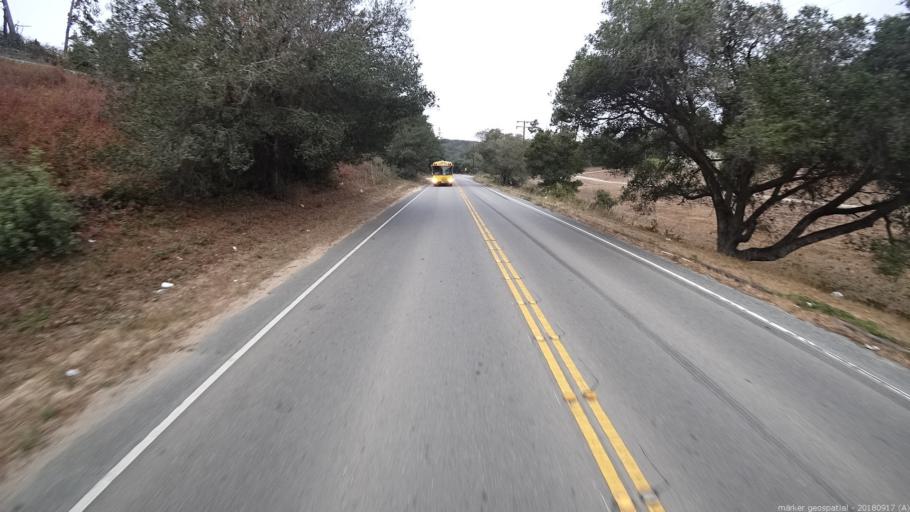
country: US
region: California
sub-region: Monterey County
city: Prunedale
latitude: 36.8001
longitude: -121.6942
